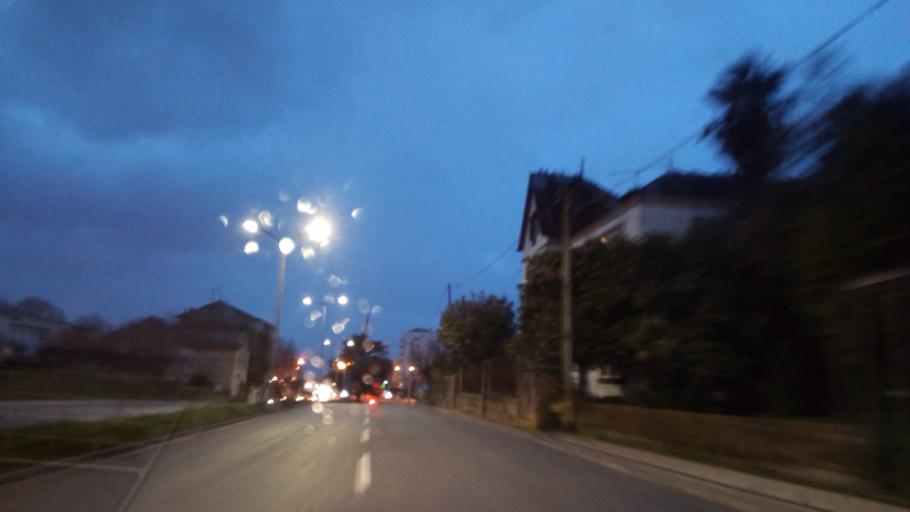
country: PT
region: Viseu
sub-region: Viseu
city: Viseu
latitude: 40.6510
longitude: -7.9130
